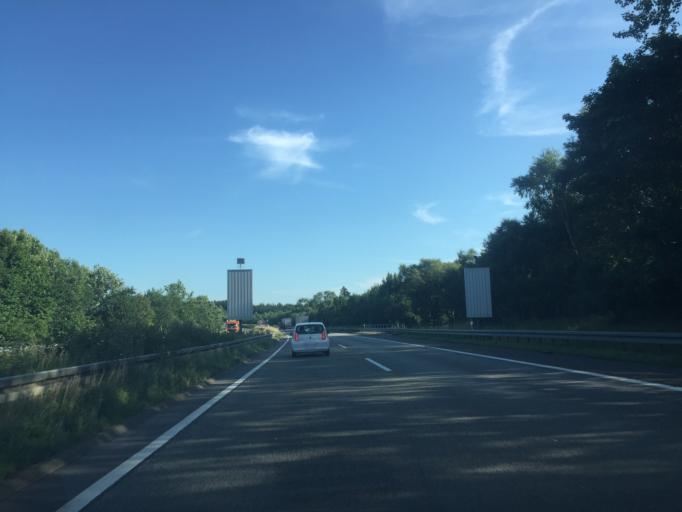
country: DE
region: North Rhine-Westphalia
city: Meinerzhagen
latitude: 51.1426
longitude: 7.6758
